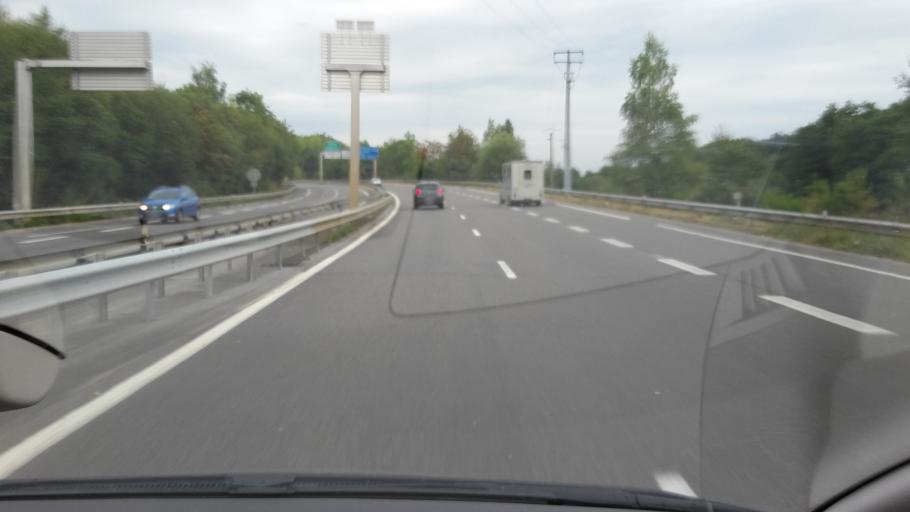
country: FR
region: Champagne-Ardenne
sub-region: Departement des Ardennes
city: La Francheville
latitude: 49.7286
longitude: 4.7171
